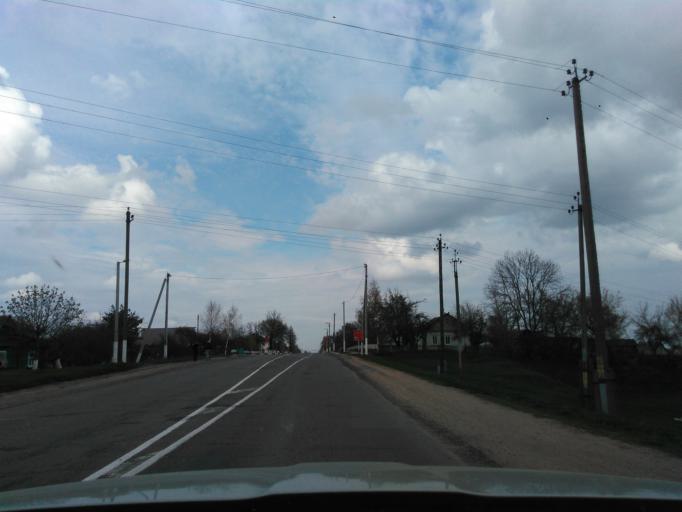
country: BY
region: Vitebsk
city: Chashniki
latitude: 54.8422
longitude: 29.1772
